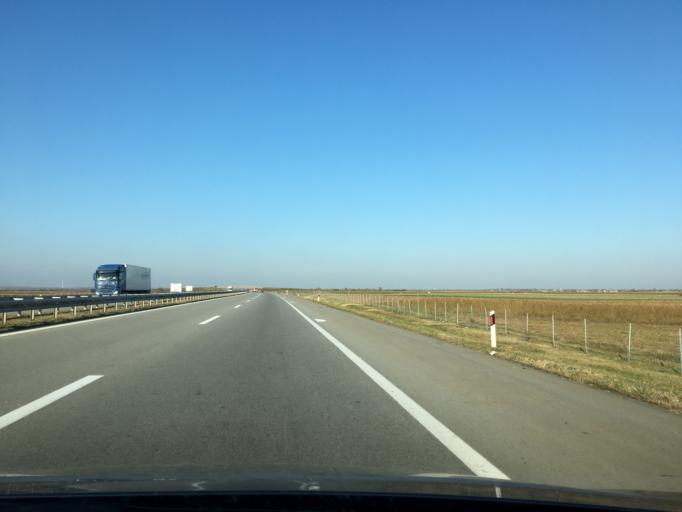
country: RS
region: Autonomna Pokrajina Vojvodina
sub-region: Juznobacki Okrug
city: Kovilj
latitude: 45.2554
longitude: 20.0080
